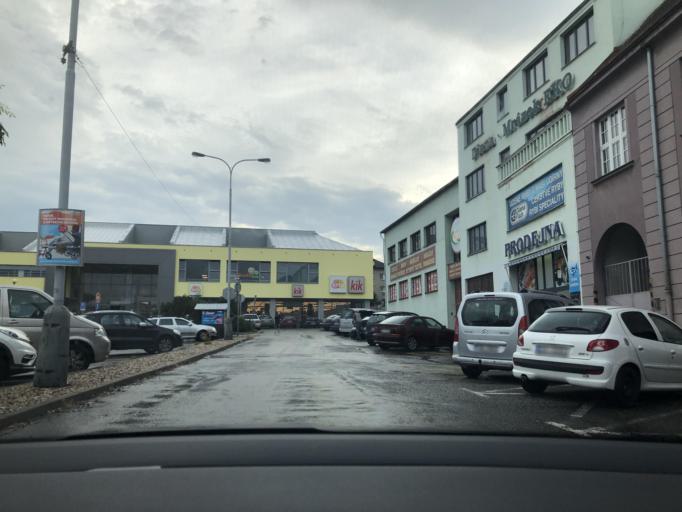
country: CZ
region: Central Bohemia
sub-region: Okres Kolin
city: Kolin
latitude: 50.0284
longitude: 15.1971
